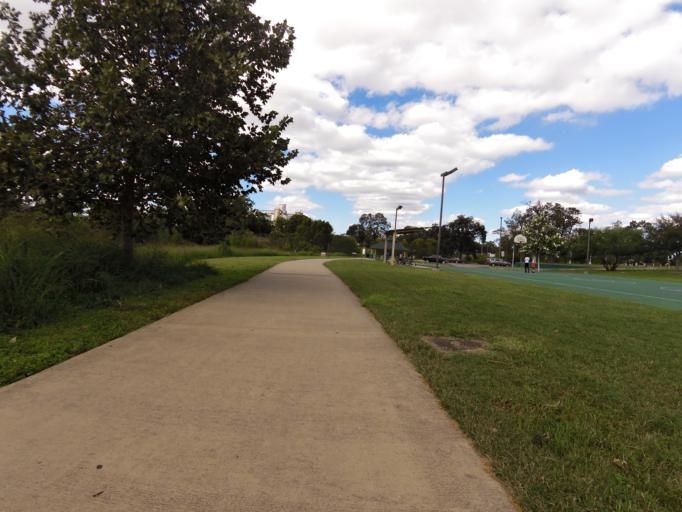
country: US
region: Texas
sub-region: Bexar County
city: San Antonio
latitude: 29.3998
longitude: -98.4888
